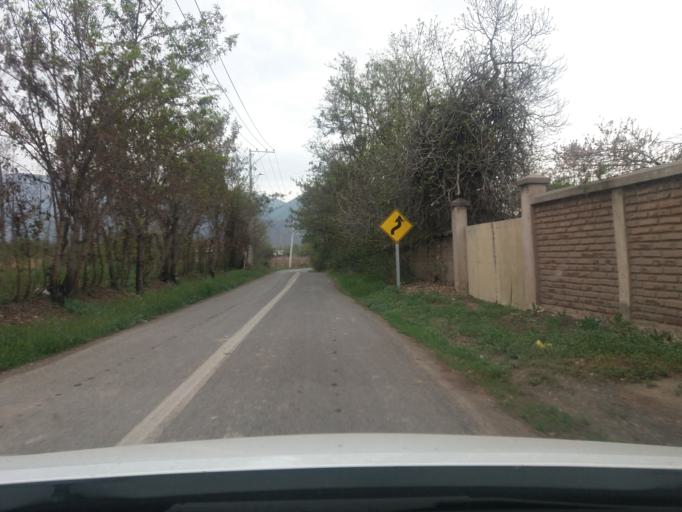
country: CL
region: Valparaiso
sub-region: Provincia de Los Andes
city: Los Andes
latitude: -32.8540
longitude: -70.6452
